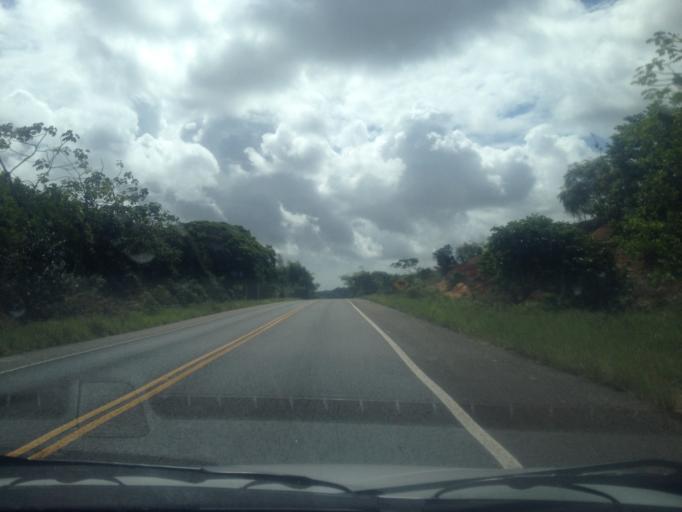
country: BR
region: Bahia
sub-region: Entre Rios
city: Entre Rios
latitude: -12.2076
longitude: -37.8266
